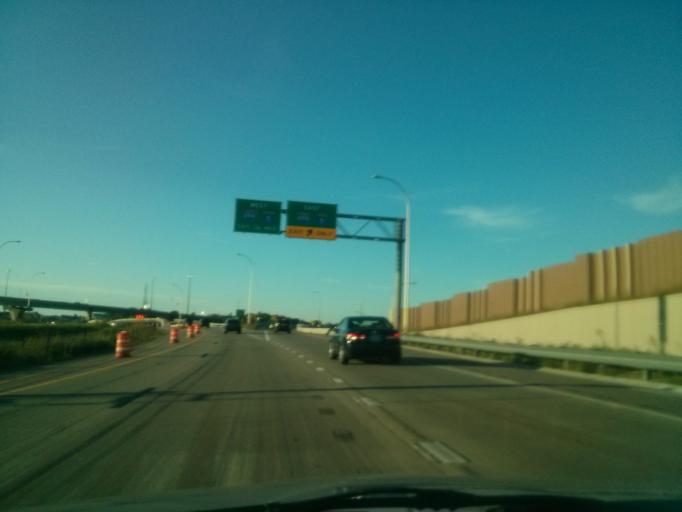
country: US
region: Minnesota
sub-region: Hennepin County
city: Edina
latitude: 44.8563
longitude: -93.3935
